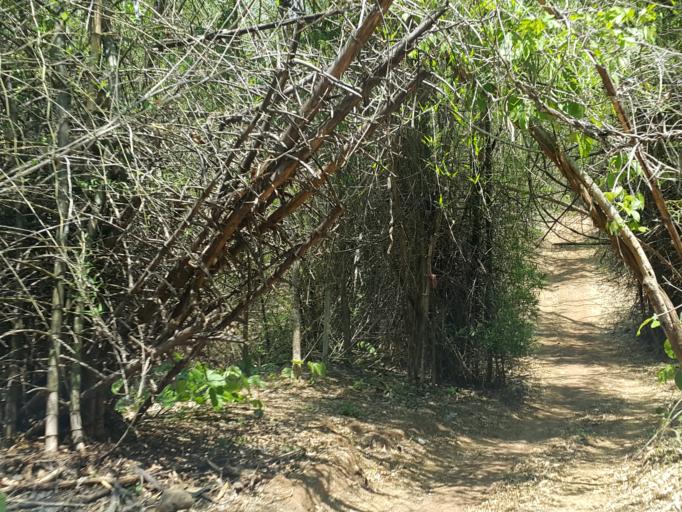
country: TH
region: Kanchanaburi
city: Sai Yok
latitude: 14.2105
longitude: 98.8813
